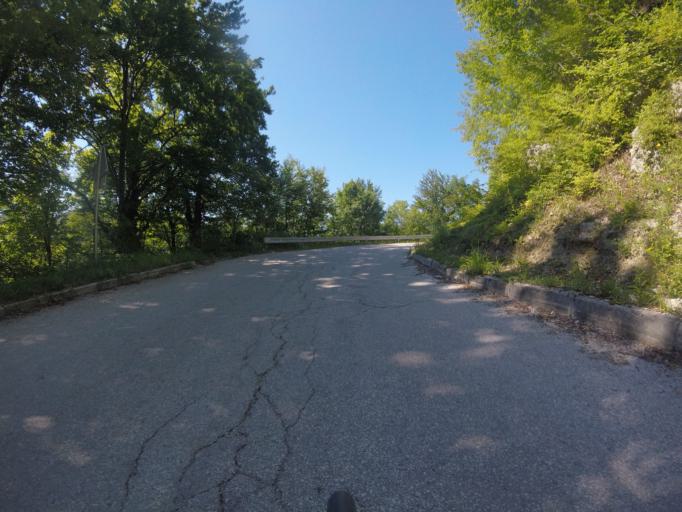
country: SI
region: Brezice
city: Brezice
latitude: 45.8374
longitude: 15.5901
